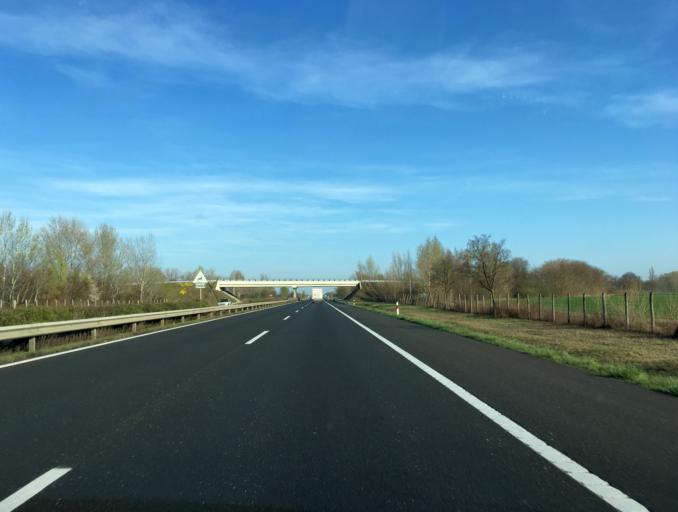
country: HU
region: Gyor-Moson-Sopron
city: Lebeny
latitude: 47.7729
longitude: 17.3682
